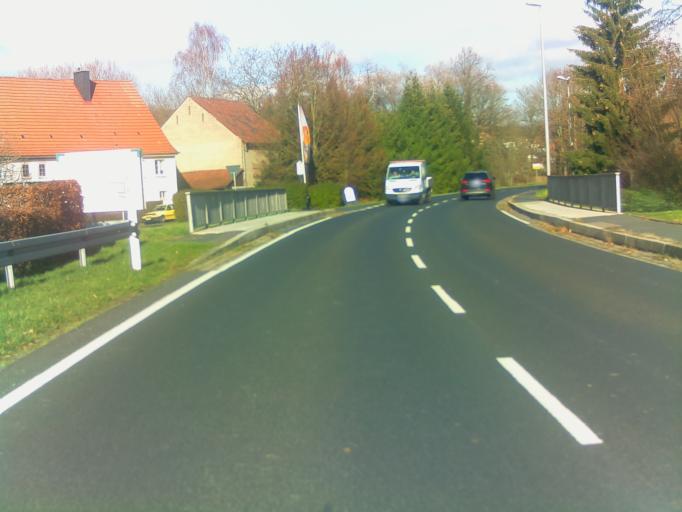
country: DE
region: Bavaria
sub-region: Regierungsbezirk Unterfranken
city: Bad Kissingen
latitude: 50.2303
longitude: 10.0680
